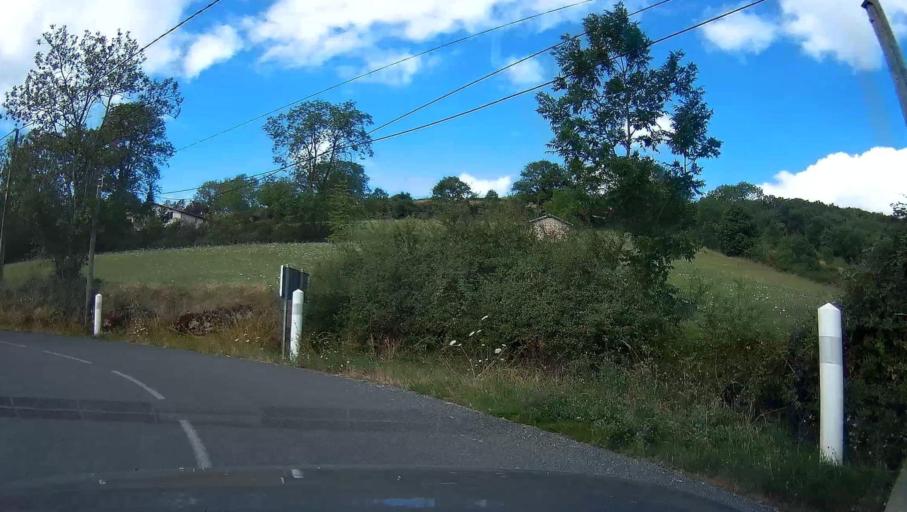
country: FR
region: Rhone-Alpes
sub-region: Departement du Rhone
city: Cogny
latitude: 45.9838
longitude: 4.5858
